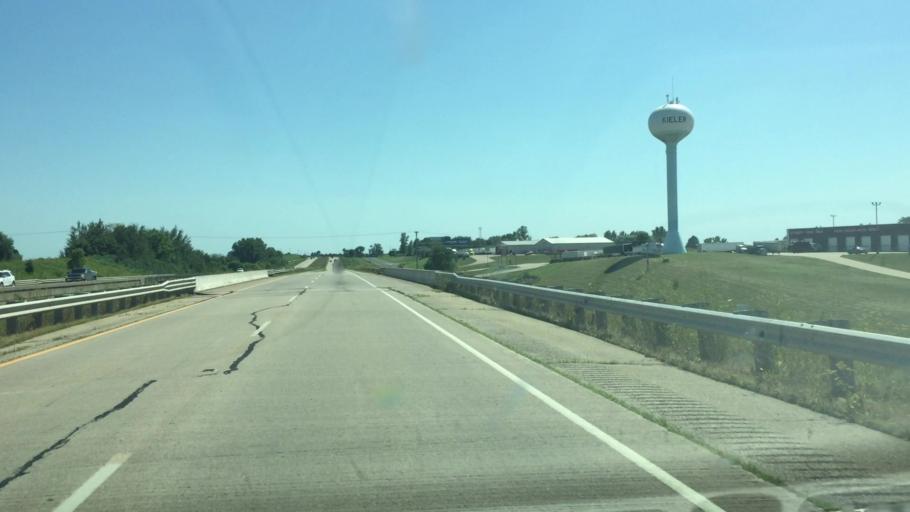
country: US
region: Wisconsin
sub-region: Grant County
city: Dickeyville
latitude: 42.5891
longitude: -90.6025
